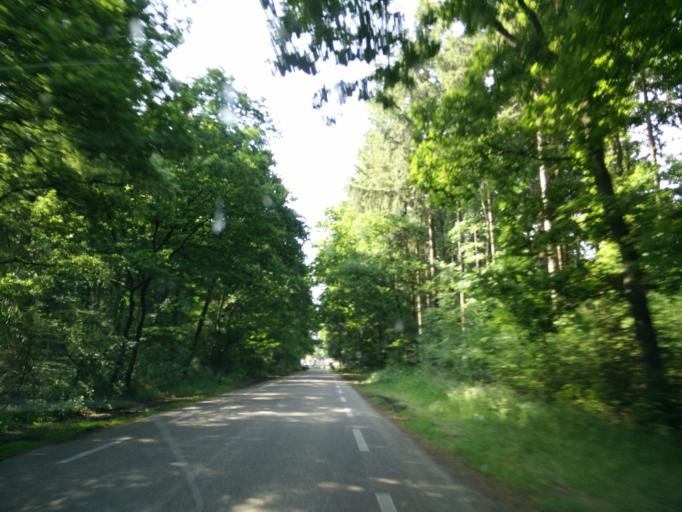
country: NL
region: Drenthe
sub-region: Gemeente Borger-Odoorn
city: Borger
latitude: 52.9606
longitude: 6.7883
